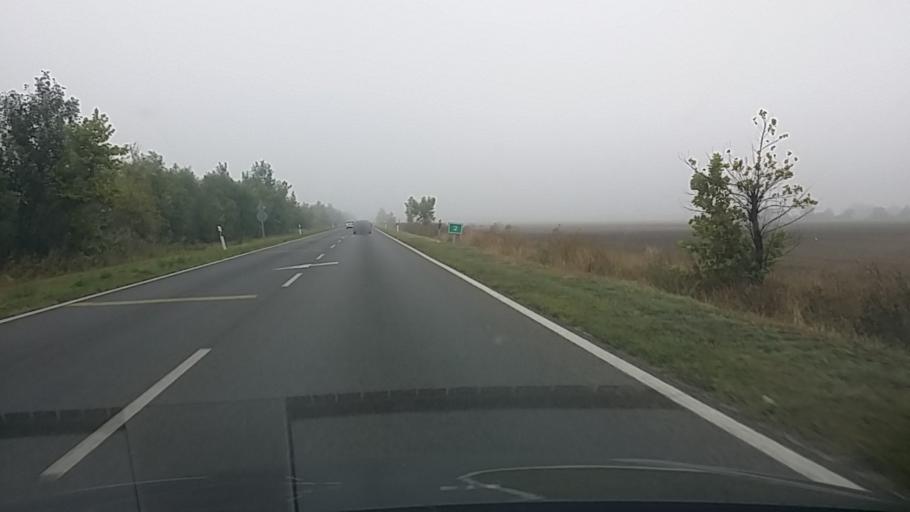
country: HU
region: Csongrad
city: Szeged
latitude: 46.2506
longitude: 20.0822
